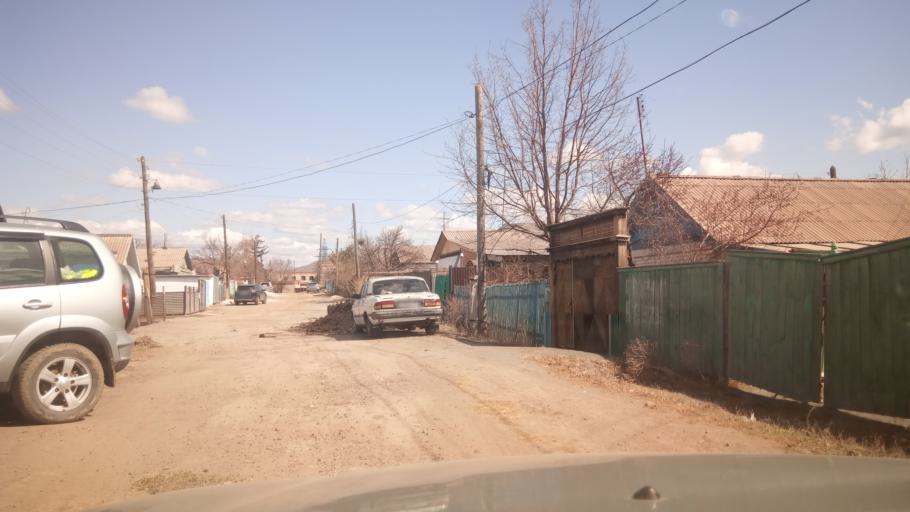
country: RU
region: Orenburg
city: Novotroitsk
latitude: 51.2085
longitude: 58.3166
